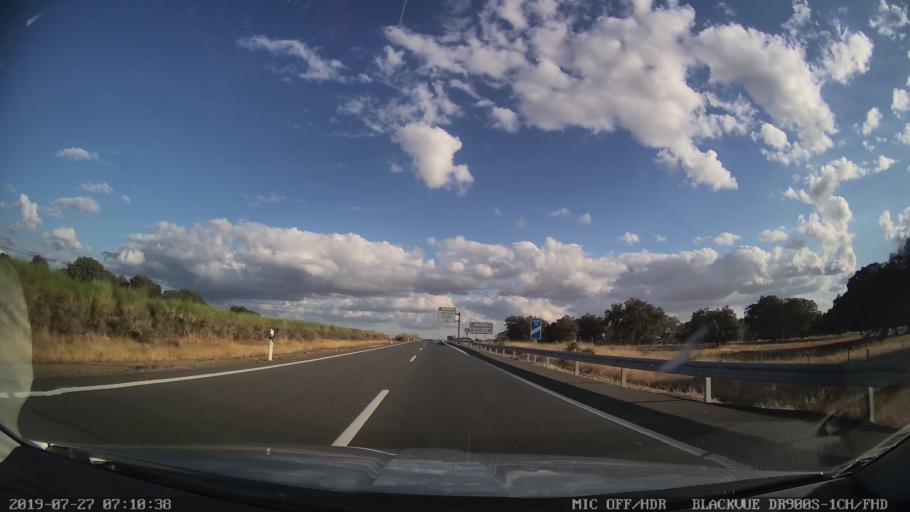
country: ES
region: Extremadura
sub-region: Provincia de Caceres
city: Torrecillas de la Tiesa
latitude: 39.5703
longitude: -5.8341
